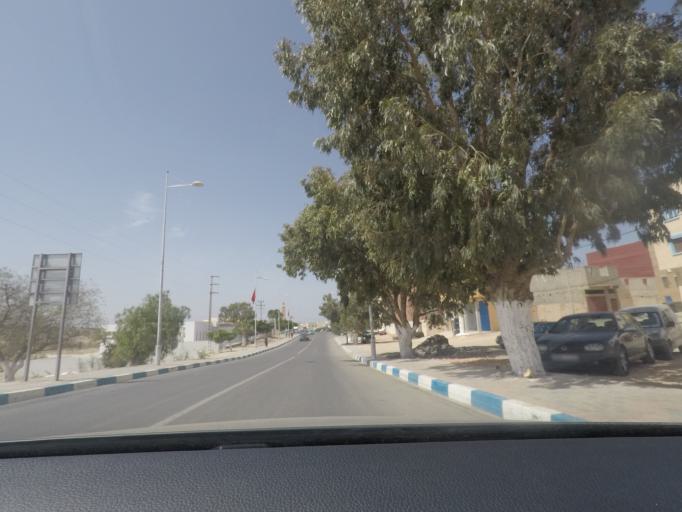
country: MA
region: Marrakech-Tensift-Al Haouz
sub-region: Essaouira
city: Tamanar
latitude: 31.0049
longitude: -9.6754
